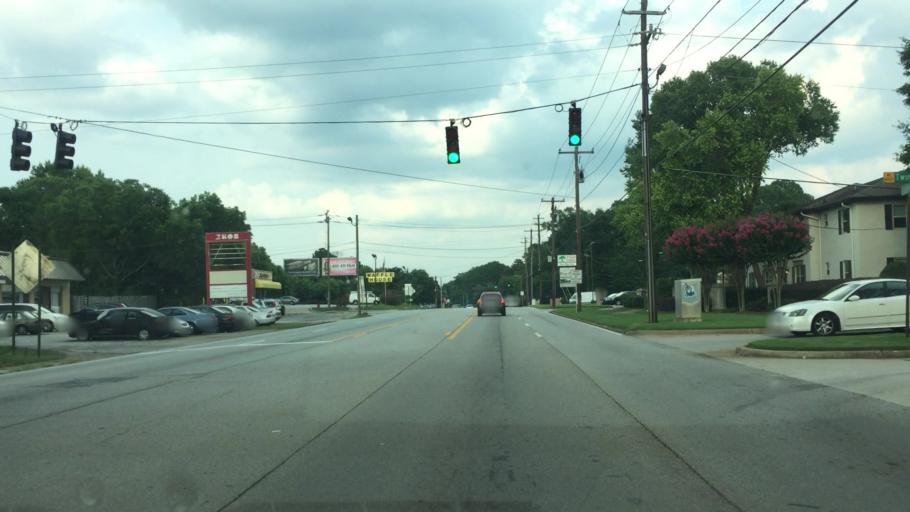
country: US
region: Georgia
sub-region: DeKalb County
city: Avondale Estates
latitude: 33.7751
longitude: -84.2753
